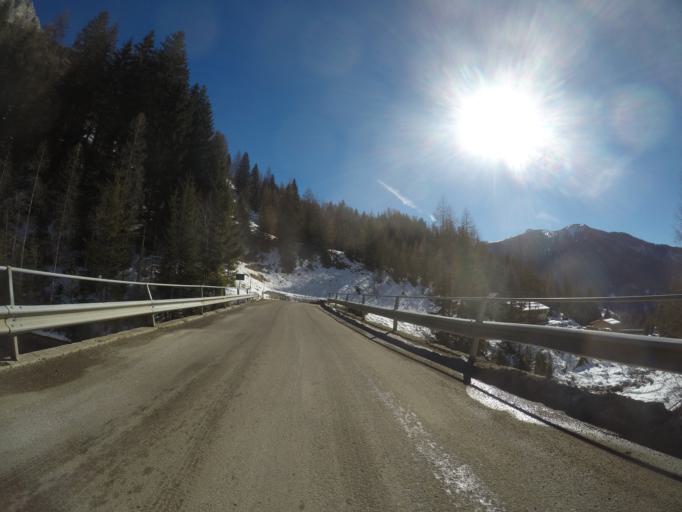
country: IT
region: Veneto
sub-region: Provincia di Belluno
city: Colle Santa Lucia
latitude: 46.4589
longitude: 12.0316
